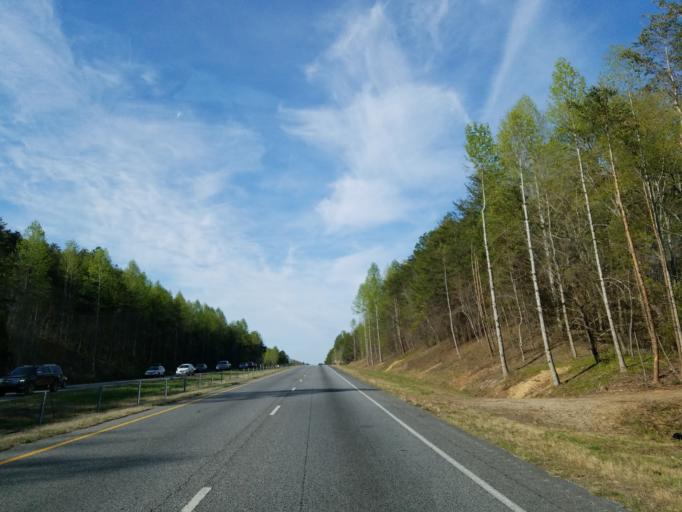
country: US
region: Georgia
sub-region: Lumpkin County
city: Dahlonega
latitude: 34.4160
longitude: -83.9926
